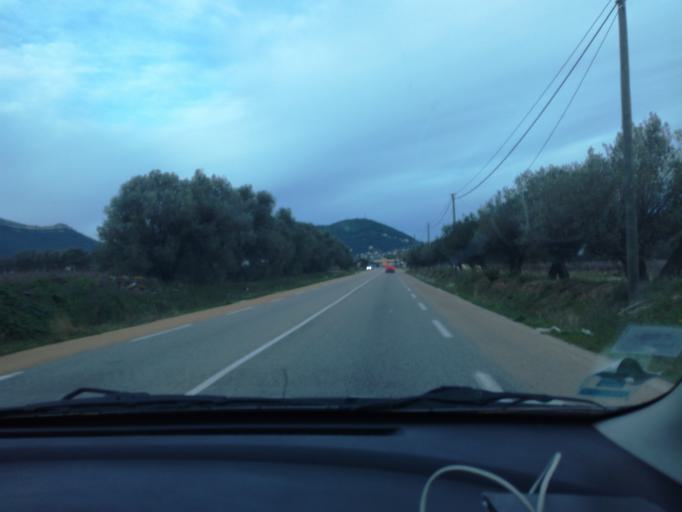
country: FR
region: Provence-Alpes-Cote d'Azur
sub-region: Departement du Var
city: La Crau
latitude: 43.1570
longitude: 6.0672
